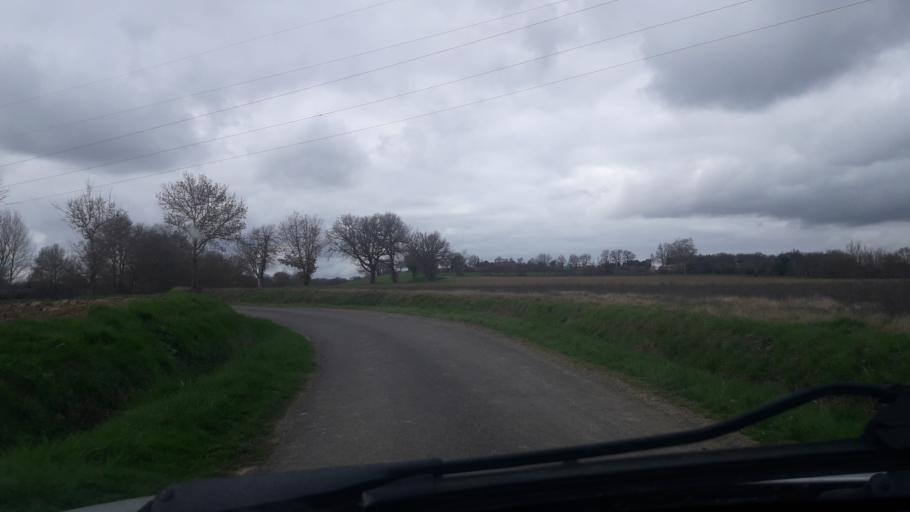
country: FR
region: Midi-Pyrenees
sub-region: Departement du Gers
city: Pujaudran
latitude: 43.6366
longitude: 1.0426
